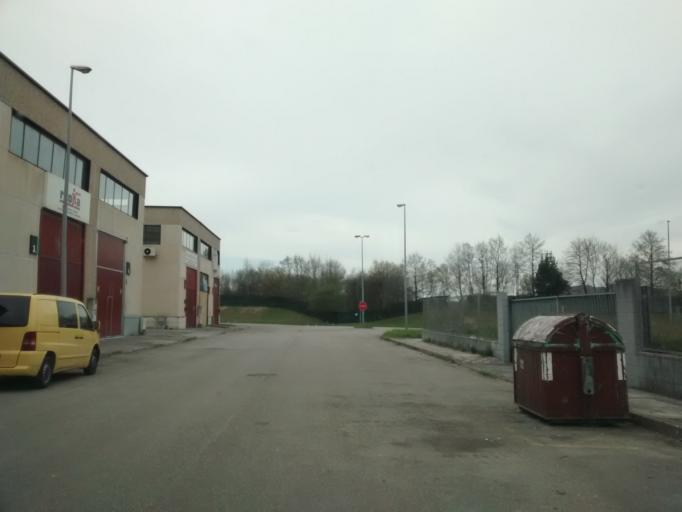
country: ES
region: Cantabria
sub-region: Provincia de Cantabria
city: El Astillero
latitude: 43.4266
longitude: -3.8434
